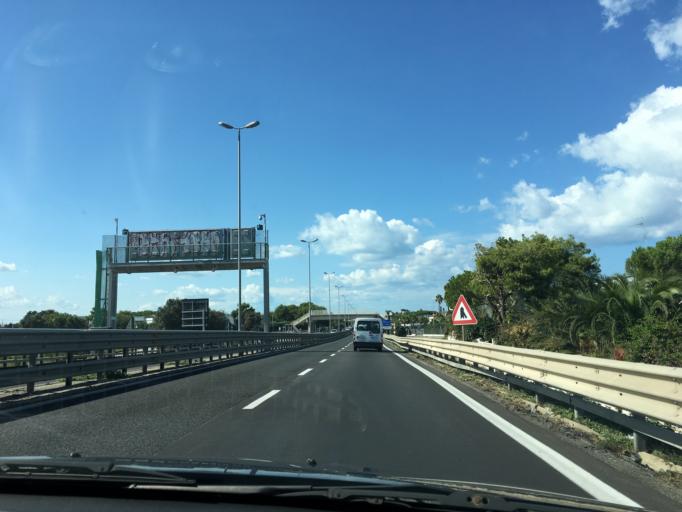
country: IT
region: Apulia
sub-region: Provincia di Bari
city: San Paolo
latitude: 41.1390
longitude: 16.8052
